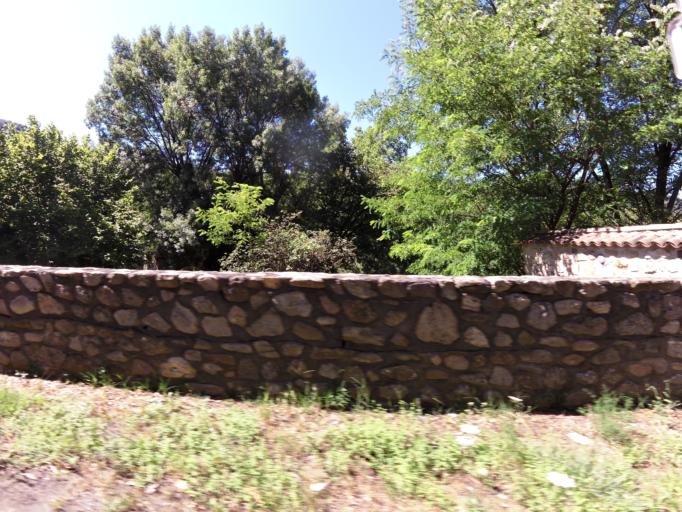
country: FR
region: Languedoc-Roussillon
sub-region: Departement du Gard
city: Saint-Jean-du-Gard
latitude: 44.0991
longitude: 3.8997
